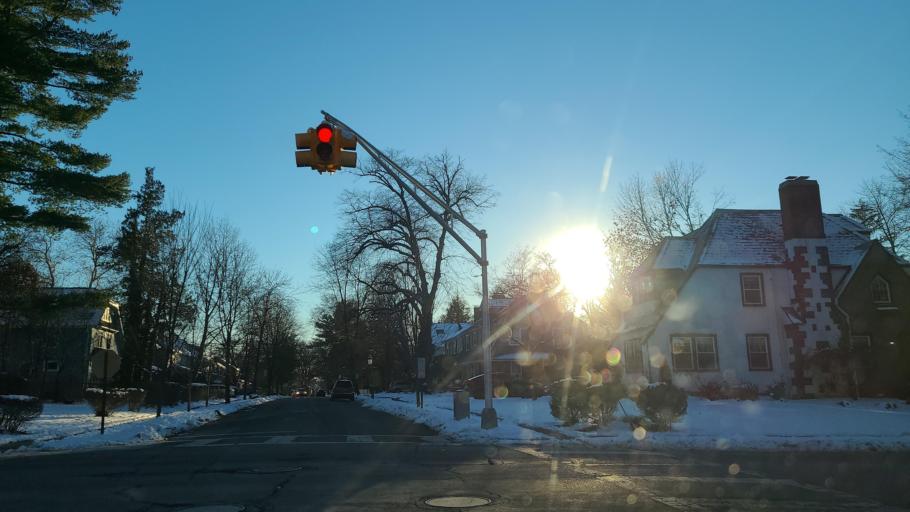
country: US
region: New Jersey
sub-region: Essex County
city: South Orange
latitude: 40.7567
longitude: -74.2545
